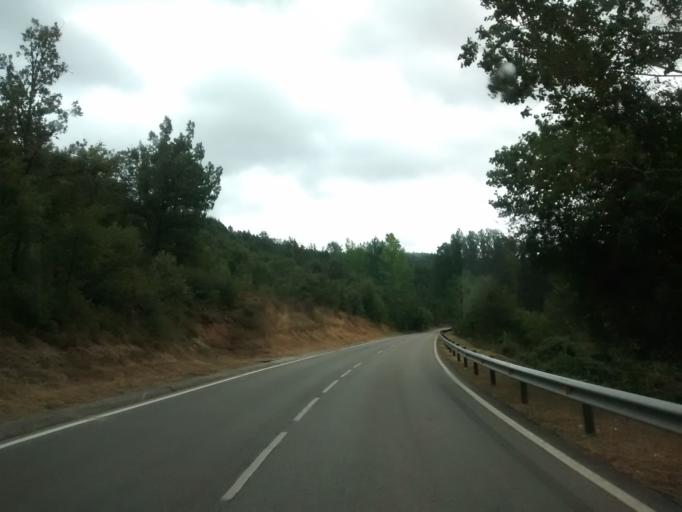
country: ES
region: Castille and Leon
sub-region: Provincia de Palencia
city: Berzosilla
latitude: 42.8036
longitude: -3.9741
